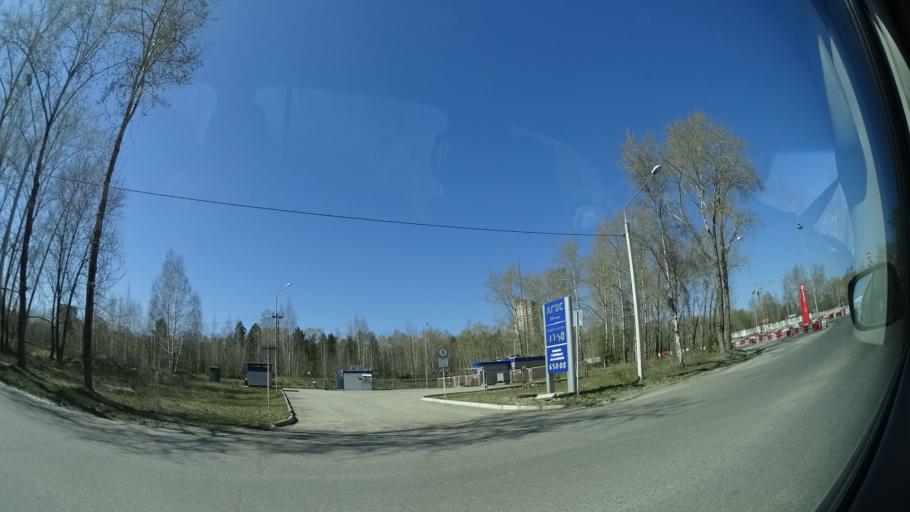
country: RU
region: Perm
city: Perm
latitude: 58.1099
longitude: 56.3228
